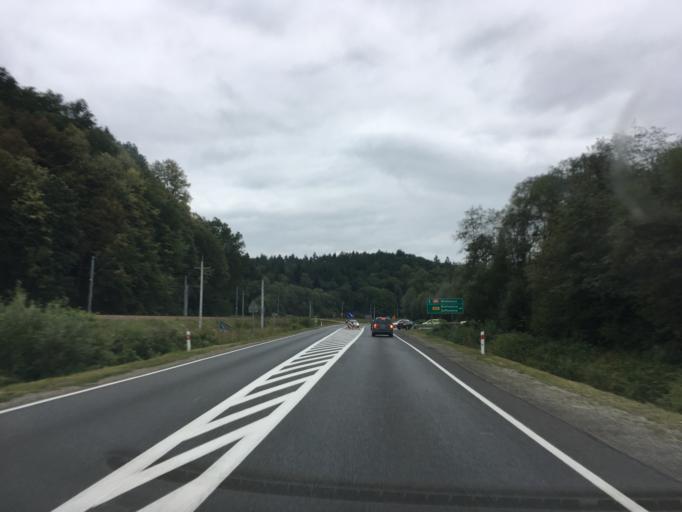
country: PL
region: Lesser Poland Voivodeship
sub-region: Powiat suski
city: Zembrzyce
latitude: 49.7652
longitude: 19.5947
